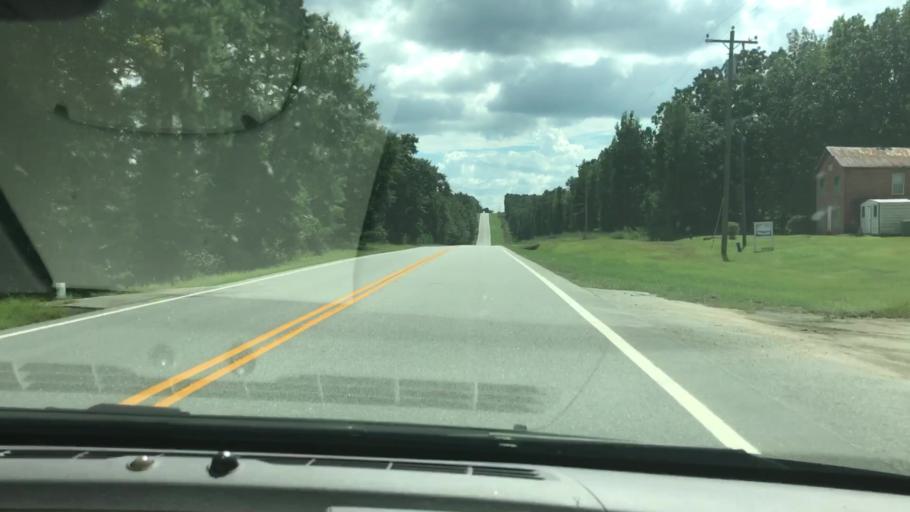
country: US
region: Georgia
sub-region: Quitman County
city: Georgetown
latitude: 31.8376
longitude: -85.0807
